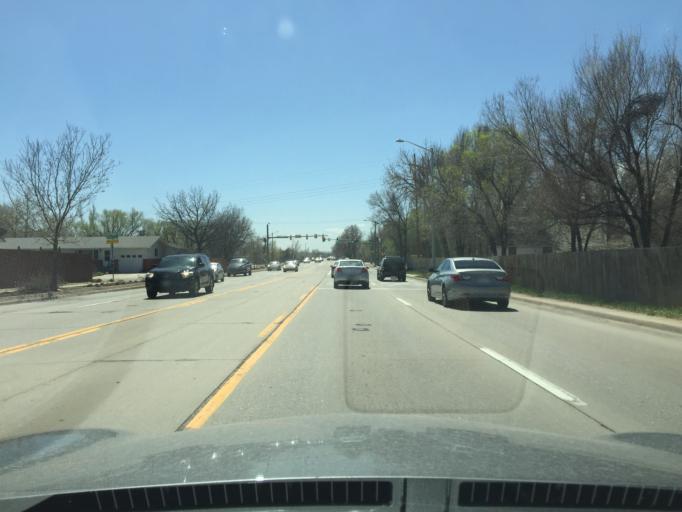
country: US
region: Colorado
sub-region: Boulder County
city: Longmont
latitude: 40.1683
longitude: -105.1309
